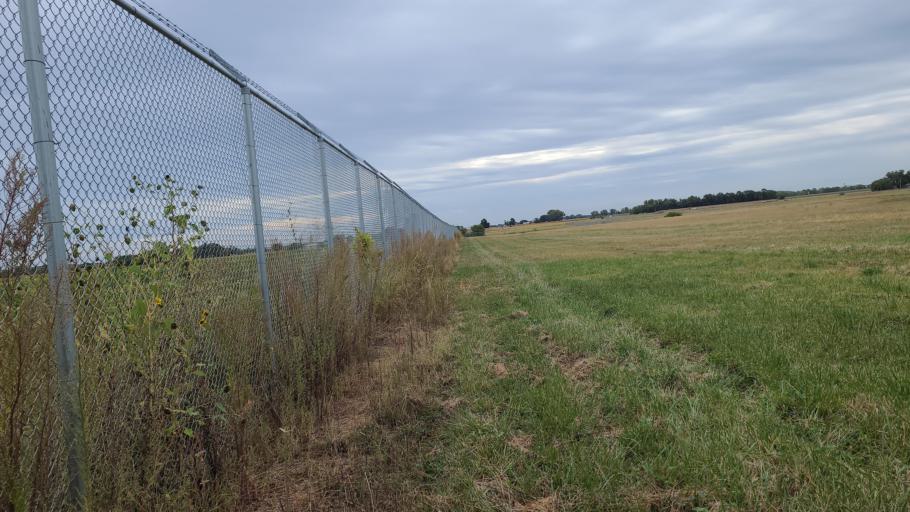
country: US
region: Kansas
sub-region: Douglas County
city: Lawrence
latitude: 39.0078
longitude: -95.2103
